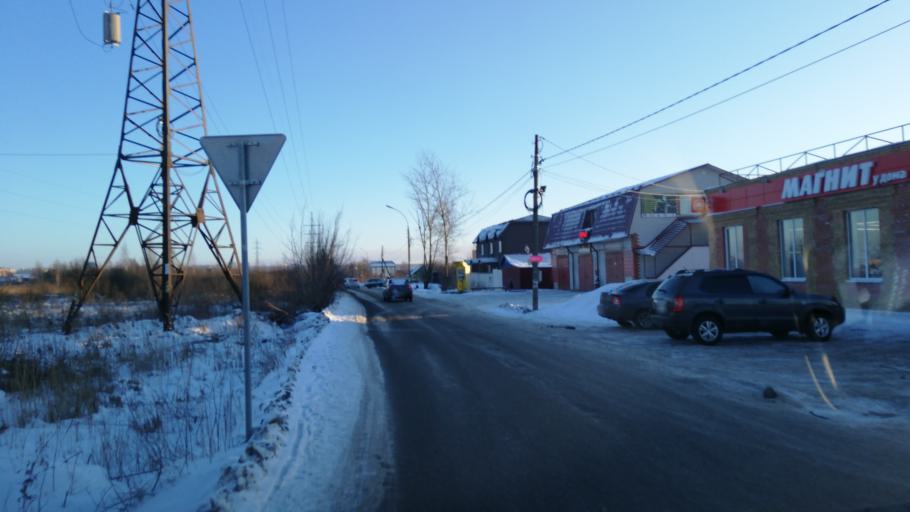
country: RU
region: Jaroslavl
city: Yaroslavl
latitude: 57.6139
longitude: 39.7909
